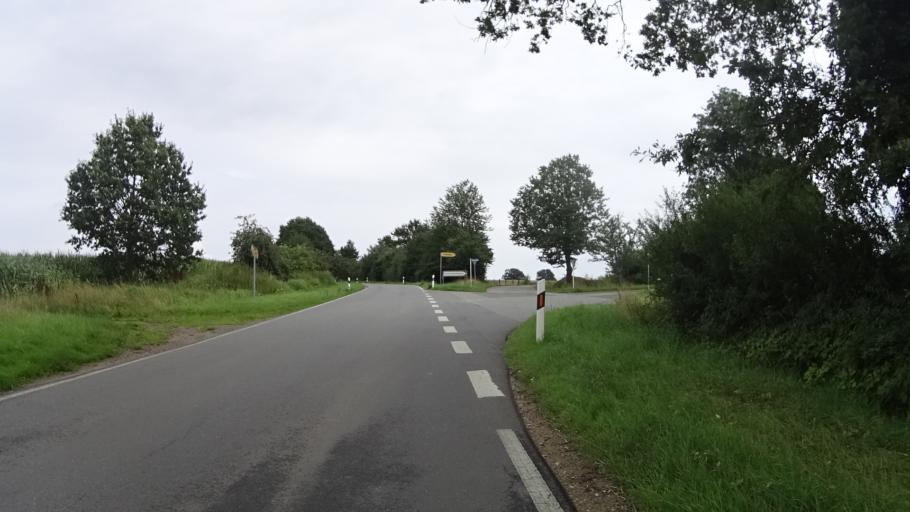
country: DE
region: Schleswig-Holstein
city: Steinhorst
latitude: 53.7143
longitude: 10.4918
